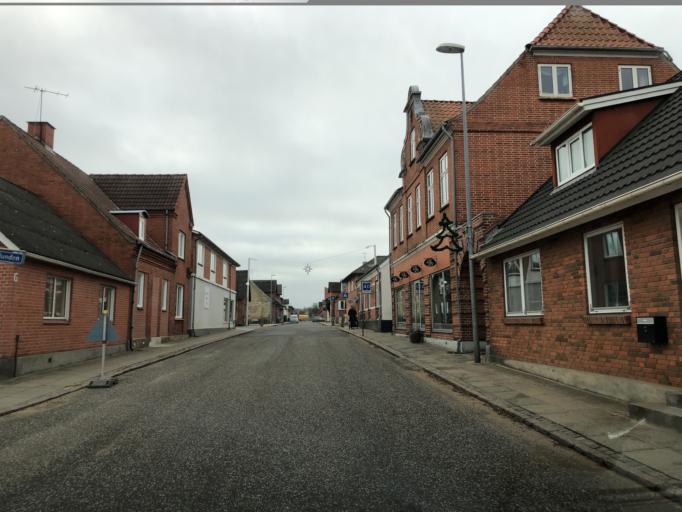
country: DK
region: Central Jutland
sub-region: Viborg Kommune
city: Stoholm
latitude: 56.4860
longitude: 9.1513
